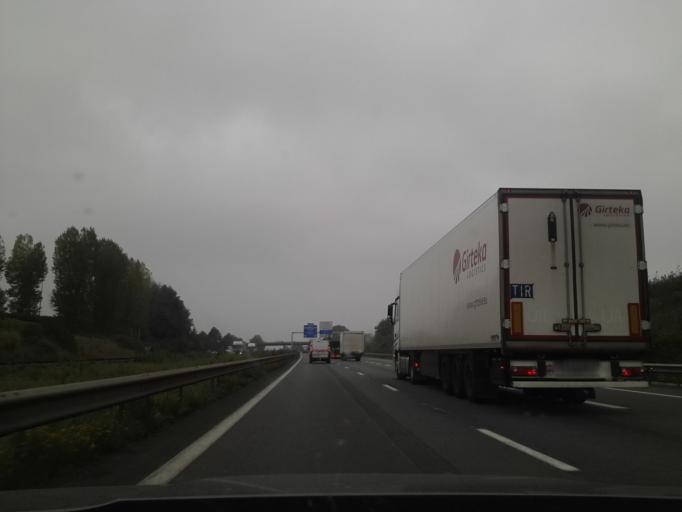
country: FR
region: Nord-Pas-de-Calais
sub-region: Departement du Nord
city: La Sentinelle
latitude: 50.3412
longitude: 3.4799
